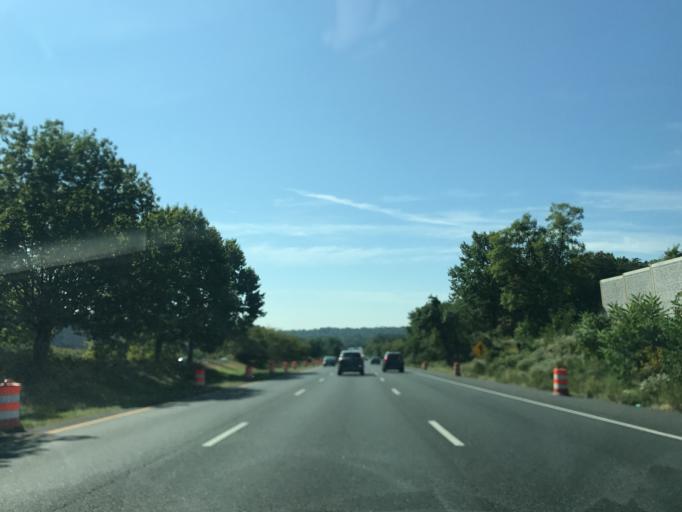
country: US
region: Maryland
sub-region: Baltimore County
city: Baltimore Highlands
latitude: 39.2354
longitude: -76.6497
